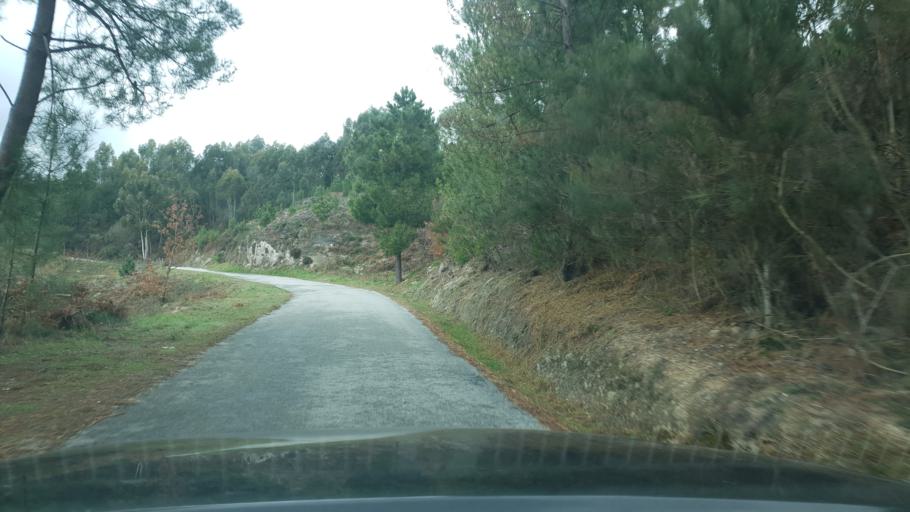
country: PT
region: Viseu
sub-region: Castro Daire
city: Castro Daire
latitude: 40.8800
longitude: -8.0019
